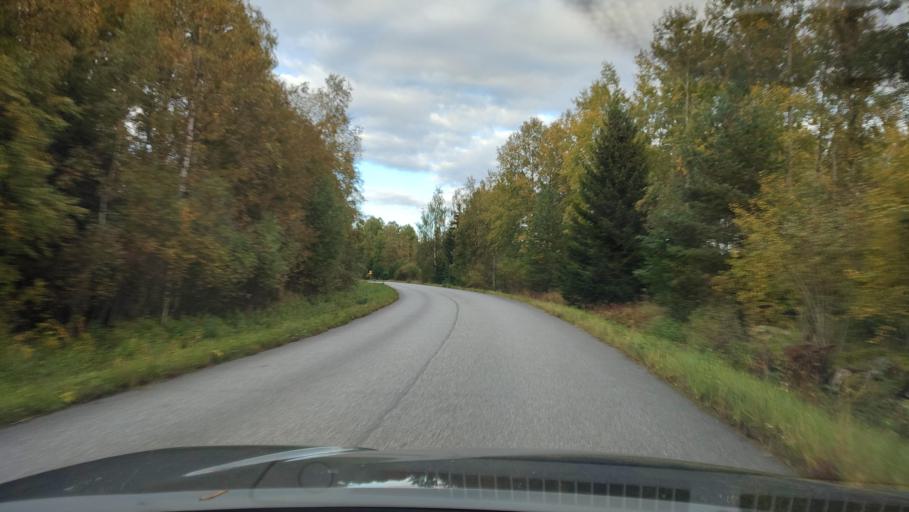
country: FI
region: Ostrobothnia
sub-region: Sydosterbotten
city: Kristinestad
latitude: 62.2895
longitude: 21.3743
